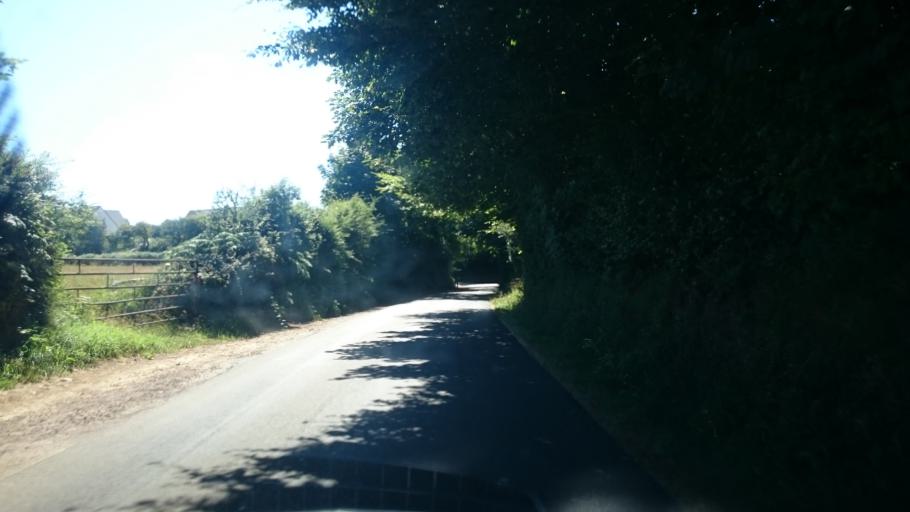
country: FR
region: Lower Normandy
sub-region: Departement de la Manche
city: Les Pieux
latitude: 49.5092
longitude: -1.8309
